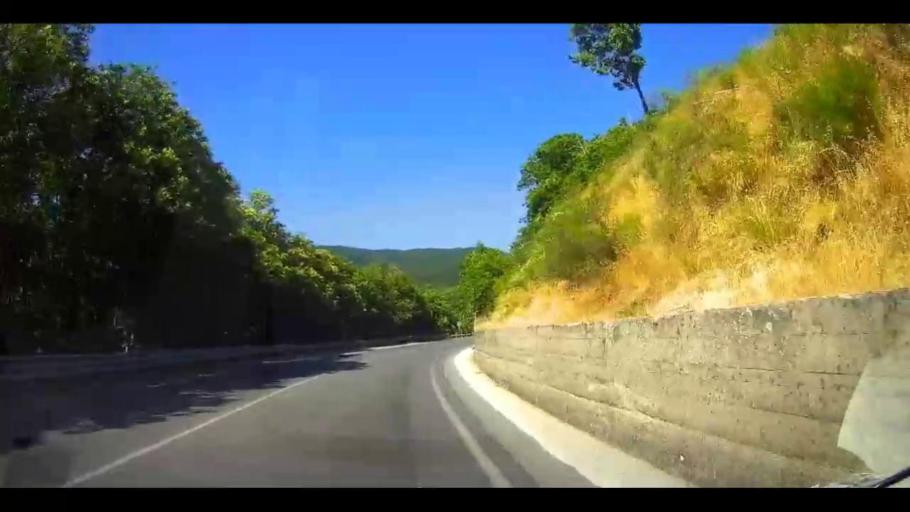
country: IT
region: Calabria
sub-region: Provincia di Cosenza
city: Celico
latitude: 39.3129
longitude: 16.3554
